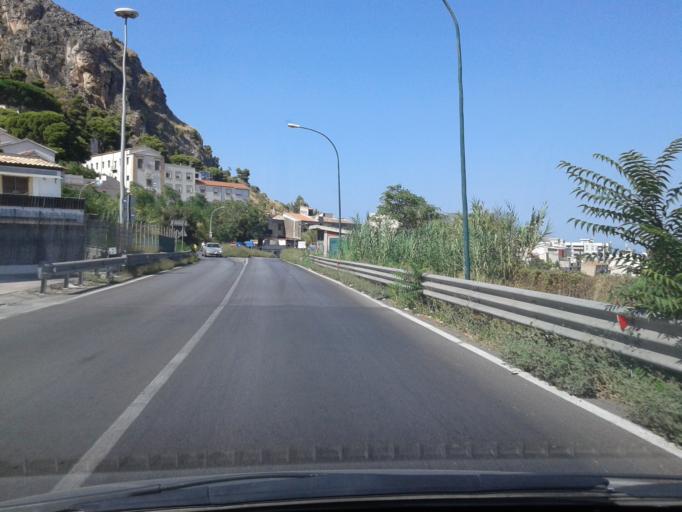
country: IT
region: Sicily
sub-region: Palermo
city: Monreale
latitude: 38.0921
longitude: 13.3068
